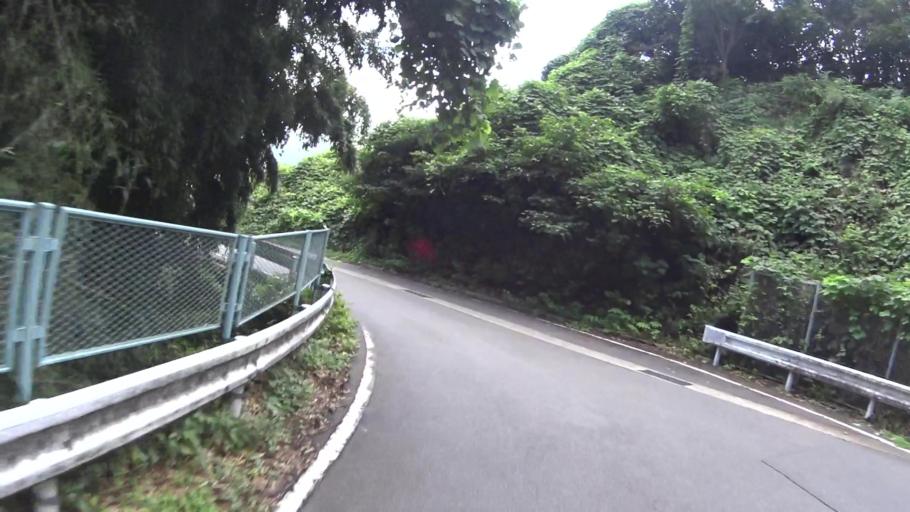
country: JP
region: Kyoto
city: Kyoto
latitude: 34.9759
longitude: 135.7907
